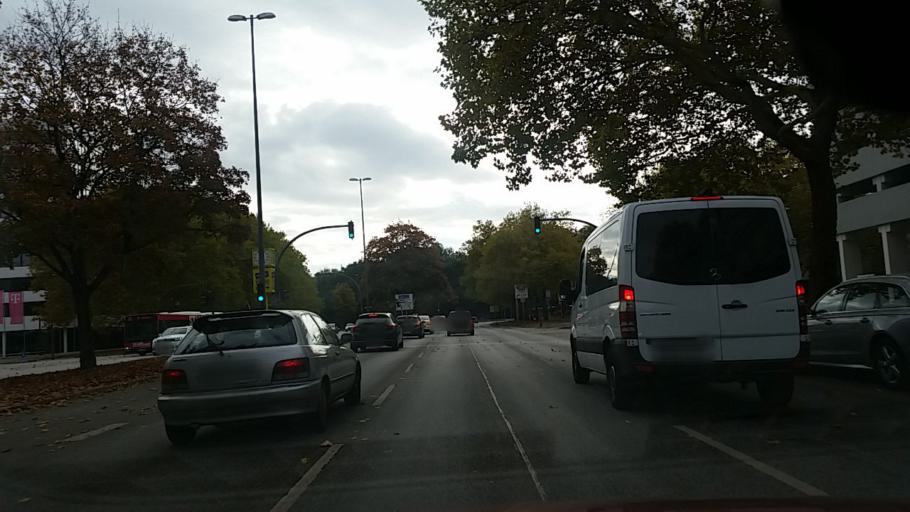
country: DE
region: Hamburg
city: Alsterdorf
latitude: 53.6022
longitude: 10.0250
